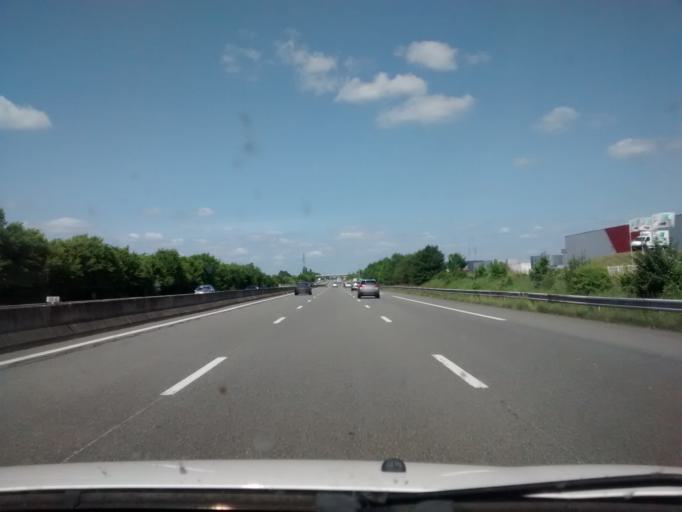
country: FR
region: Centre
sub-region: Departement d'Eure-et-Loir
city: Le Coudray
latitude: 48.4313
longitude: 1.5191
